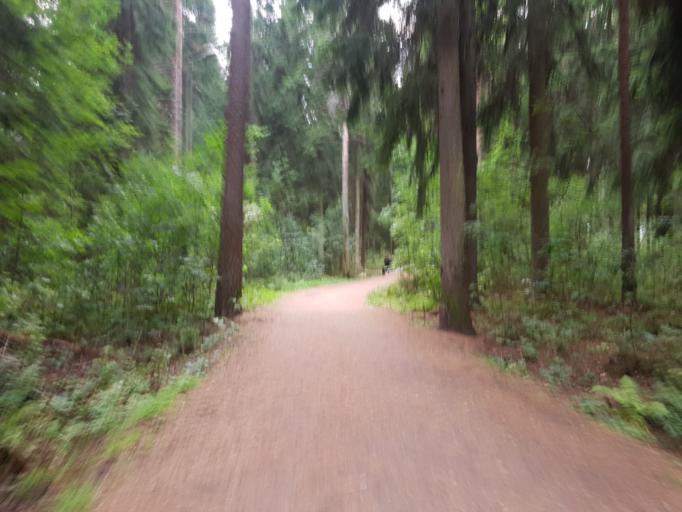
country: FI
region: Uusimaa
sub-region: Helsinki
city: Helsinki
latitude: 60.2363
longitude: 24.9541
